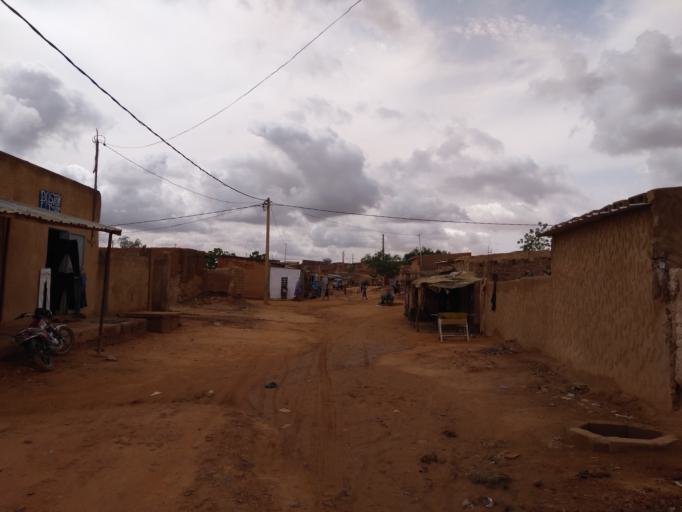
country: NE
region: Niamey
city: Niamey
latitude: 13.4825
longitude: 2.1508
